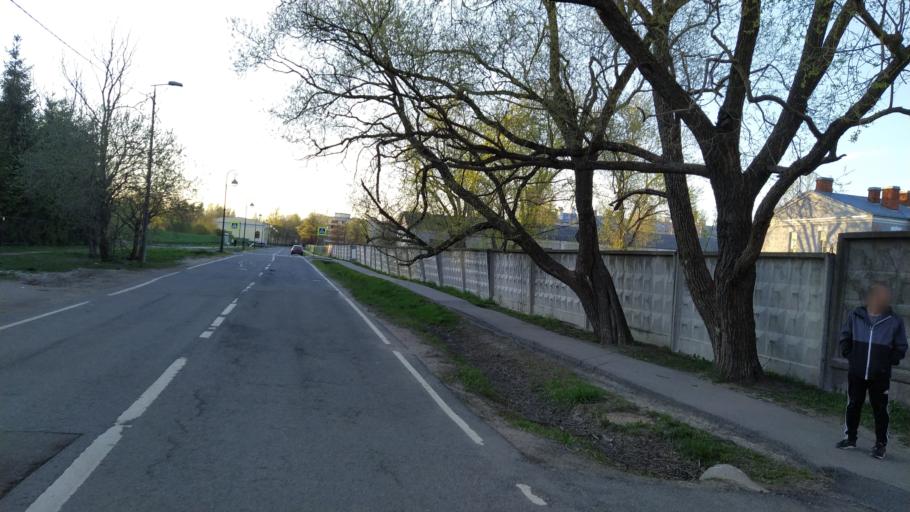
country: RU
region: St.-Petersburg
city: Pushkin
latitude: 59.7038
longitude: 30.3969
